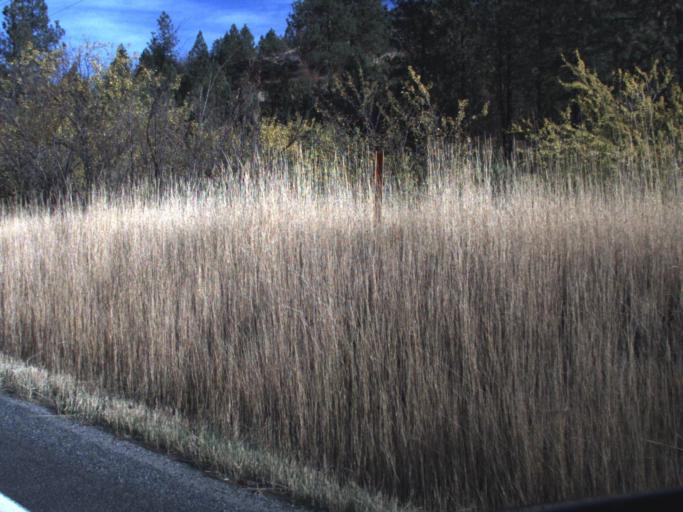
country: US
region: Washington
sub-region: Stevens County
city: Kettle Falls
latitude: 48.1469
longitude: -118.1790
